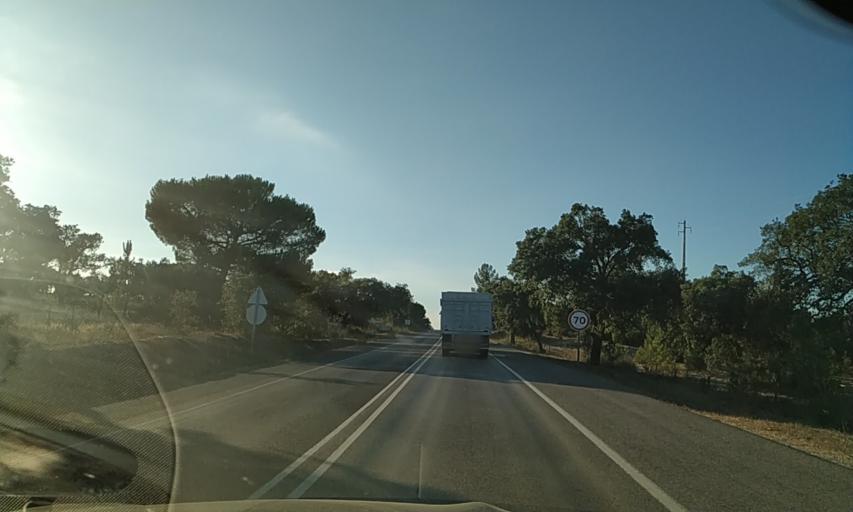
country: PT
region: Evora
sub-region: Vendas Novas
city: Vendas Novas
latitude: 38.5676
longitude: -8.6592
